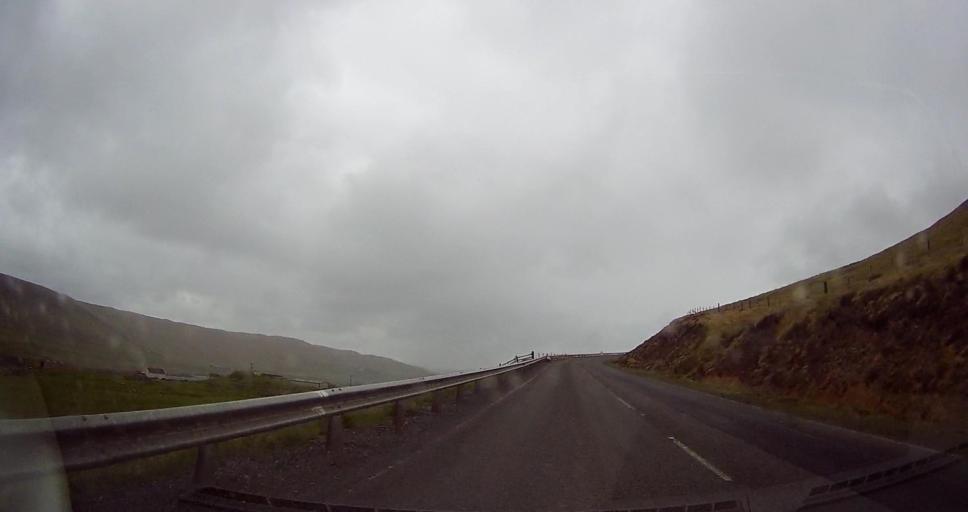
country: GB
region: Scotland
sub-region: Shetland Islands
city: Lerwick
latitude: 60.2492
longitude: -1.3012
